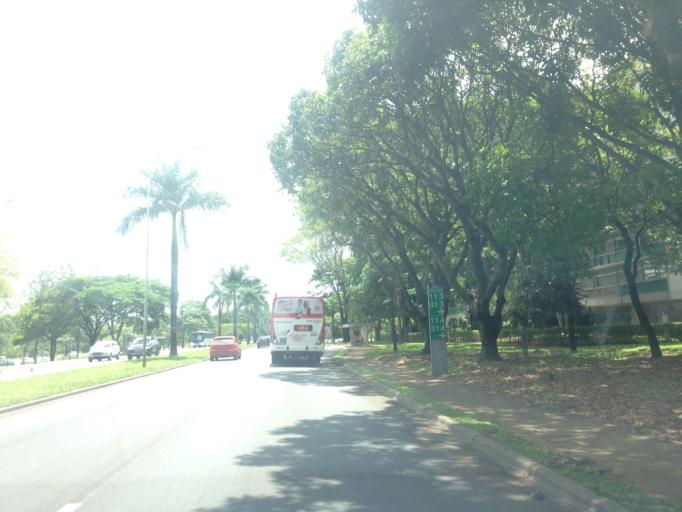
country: BR
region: Federal District
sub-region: Brasilia
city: Brasilia
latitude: -15.8273
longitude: -47.9163
